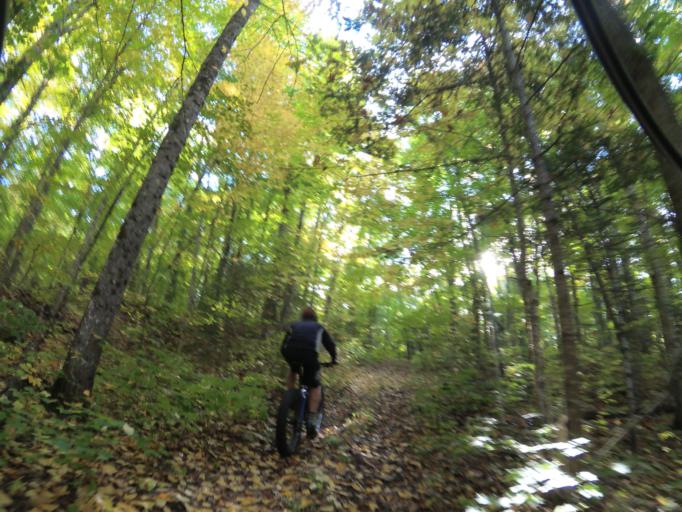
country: CA
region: Ontario
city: Pembroke
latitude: 45.3337
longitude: -77.1771
